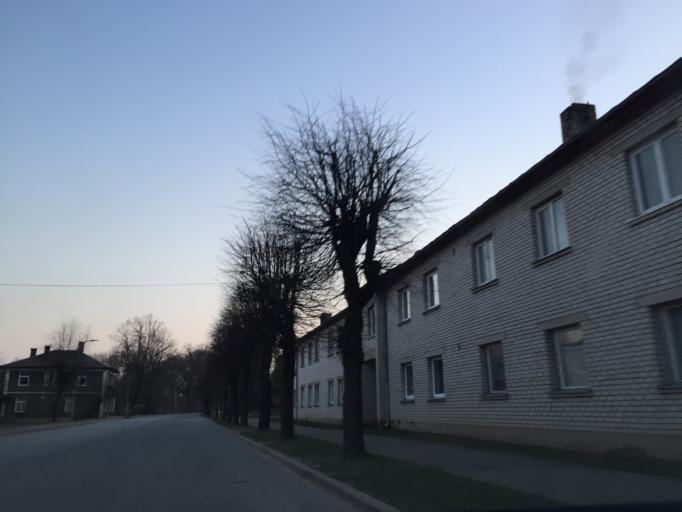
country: LV
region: Valkas Rajons
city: Valka
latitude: 57.7708
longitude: 26.0148
